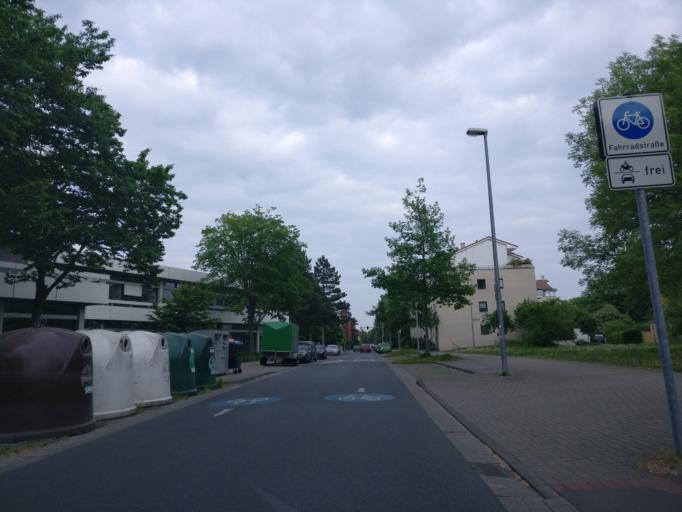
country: DE
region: Lower Saxony
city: Laatzen
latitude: 52.3323
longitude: 9.7676
